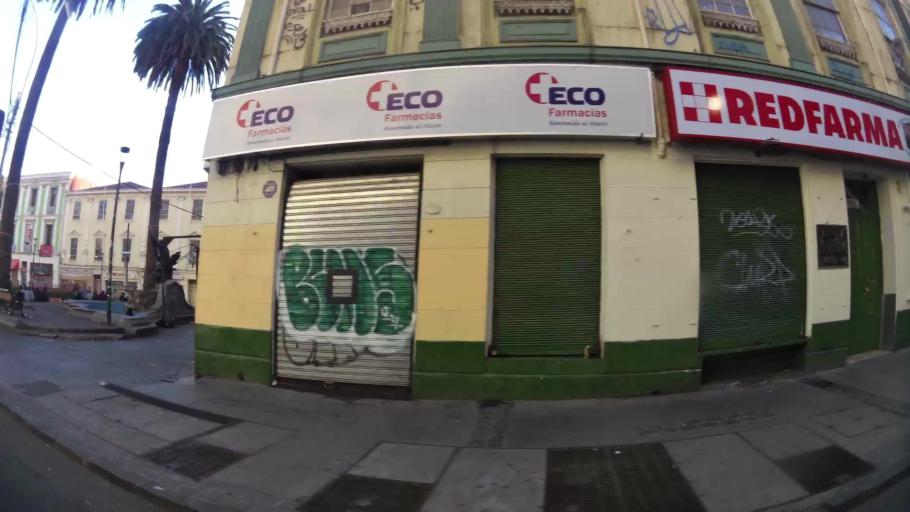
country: CL
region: Valparaiso
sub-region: Provincia de Valparaiso
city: Valparaiso
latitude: -33.0436
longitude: -71.6245
